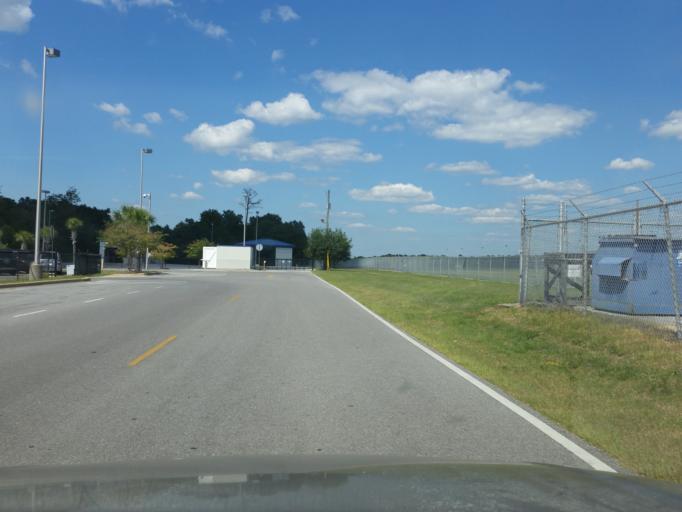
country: US
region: Florida
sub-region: Escambia County
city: Ferry Pass
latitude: 30.4801
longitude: -87.1928
